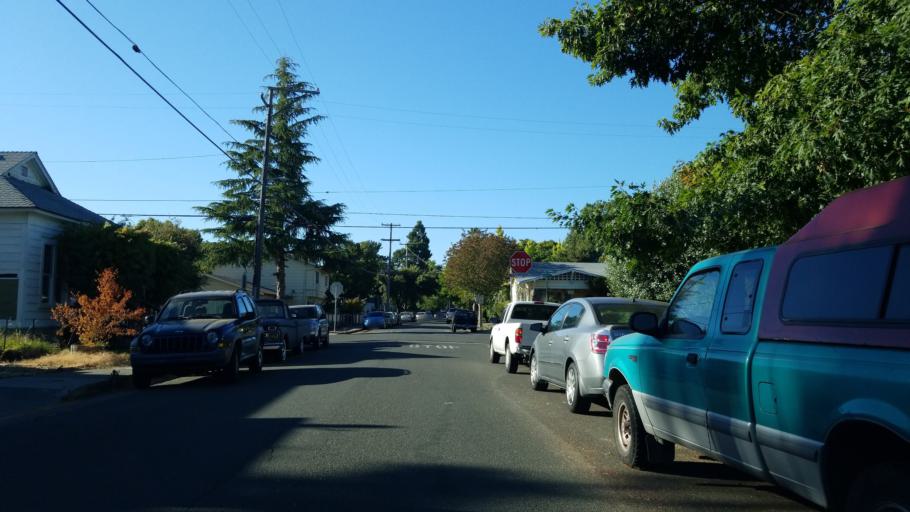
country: US
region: California
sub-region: Sonoma County
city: Santa Rosa
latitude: 38.4431
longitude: -122.7246
